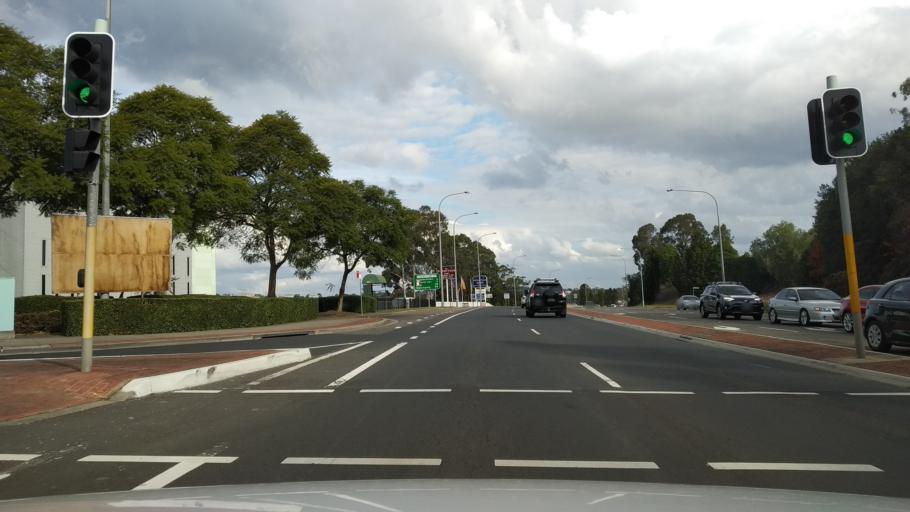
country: AU
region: New South Wales
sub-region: Campbelltown Municipality
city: Leumeah
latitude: -34.0456
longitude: 150.8295
